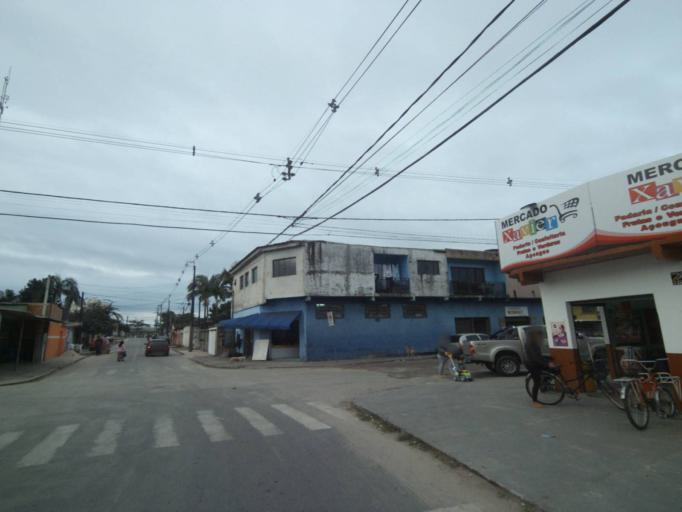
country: BR
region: Parana
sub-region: Paranagua
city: Paranagua
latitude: -25.5331
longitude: -48.5451
